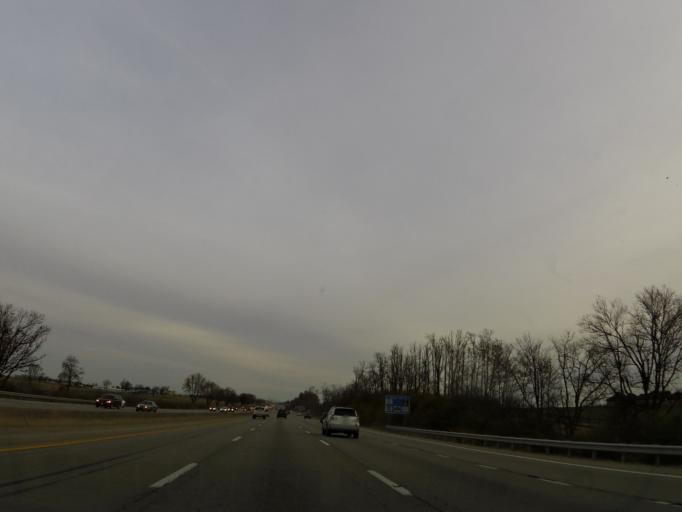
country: US
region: Kentucky
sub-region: Fayette County
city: Lexington-Fayette
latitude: 38.1078
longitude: -84.5020
